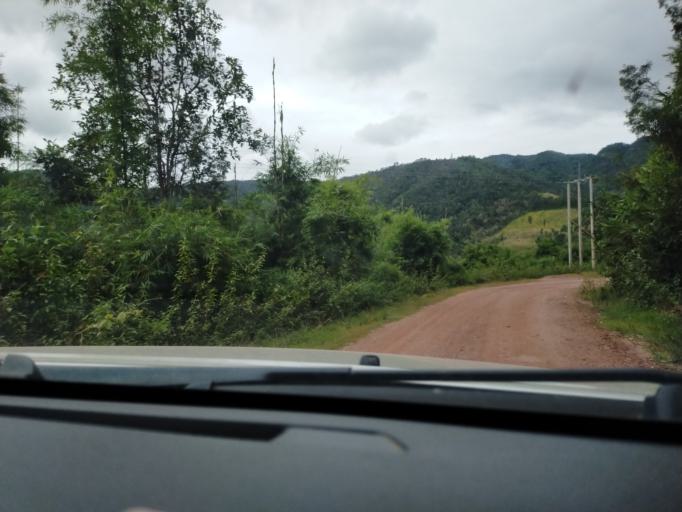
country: TH
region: Nan
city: Chaloem Phra Kiat
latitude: 19.7650
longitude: 101.3485
